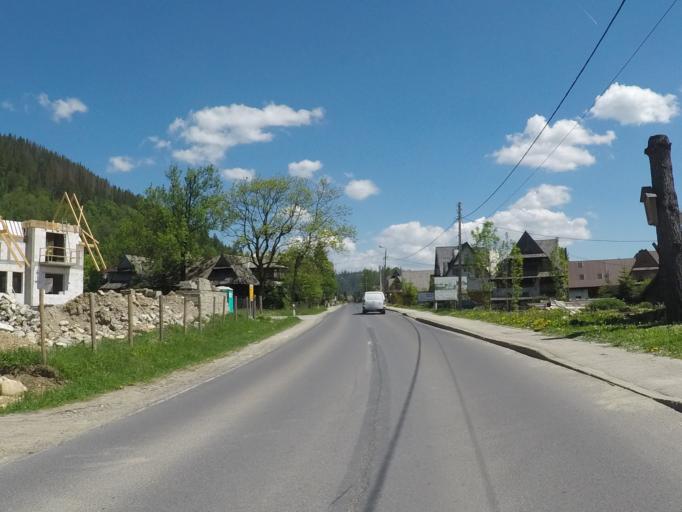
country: PL
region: Lesser Poland Voivodeship
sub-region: Powiat tatrzanski
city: Poronin
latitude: 49.3317
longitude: 20.0144
